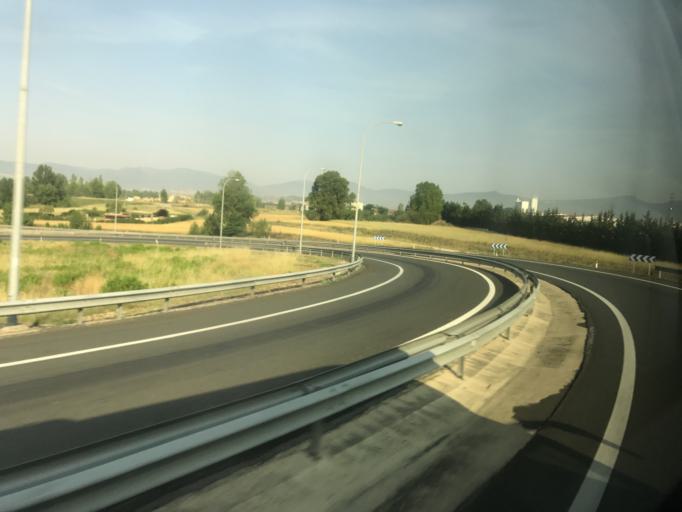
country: ES
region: Castille and Leon
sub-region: Provincia de Burgos
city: Miranda de Ebro
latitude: 42.7044
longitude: -2.9633
